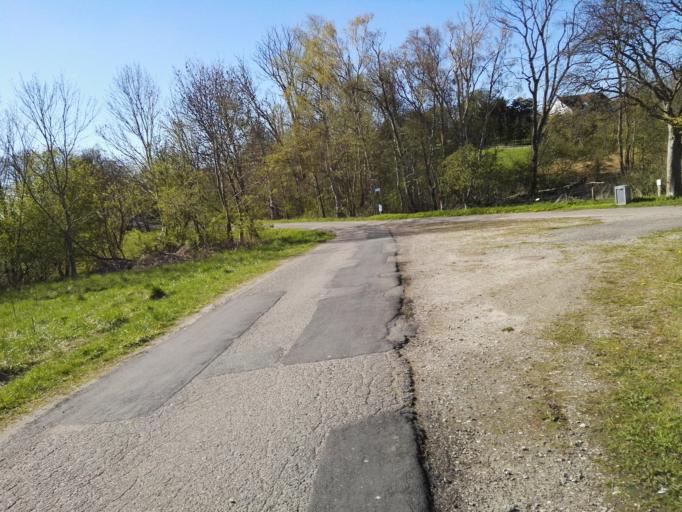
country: DK
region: Capital Region
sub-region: Egedal Kommune
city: Vekso
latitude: 55.7533
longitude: 12.2279
